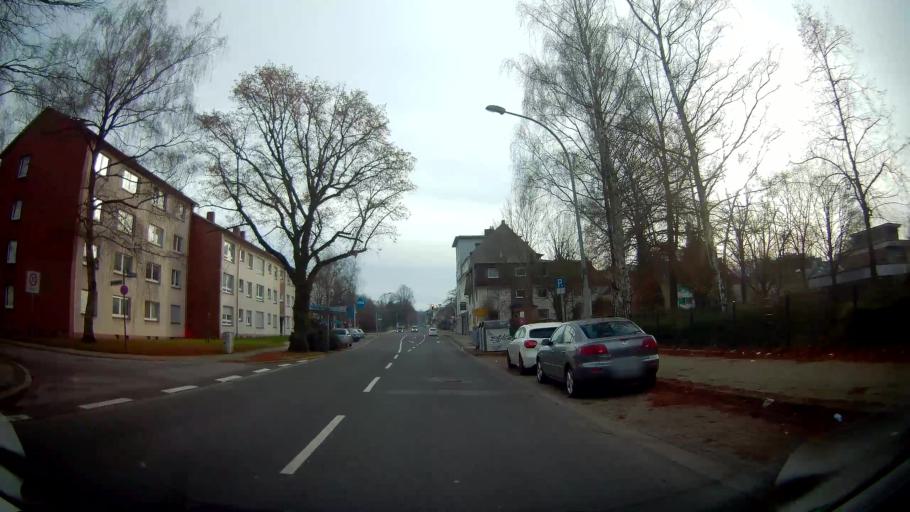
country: DE
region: North Rhine-Westphalia
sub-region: Regierungsbezirk Arnsberg
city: Herne
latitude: 51.5339
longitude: 7.2335
